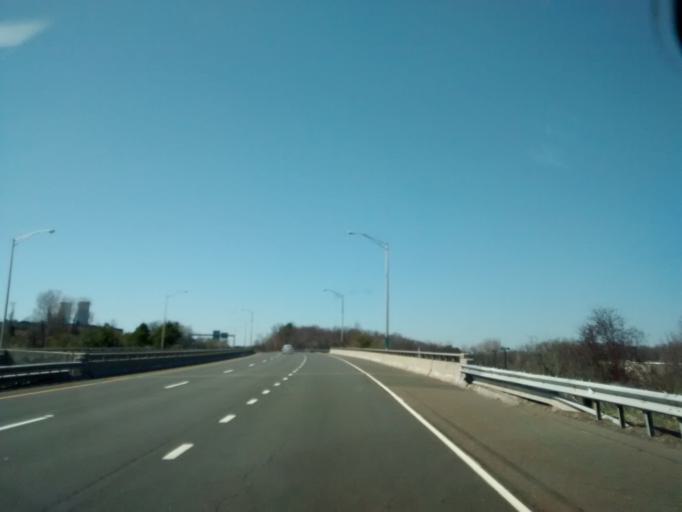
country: US
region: Connecticut
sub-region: Hartford County
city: East Hartford
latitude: 41.7926
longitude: -72.5705
